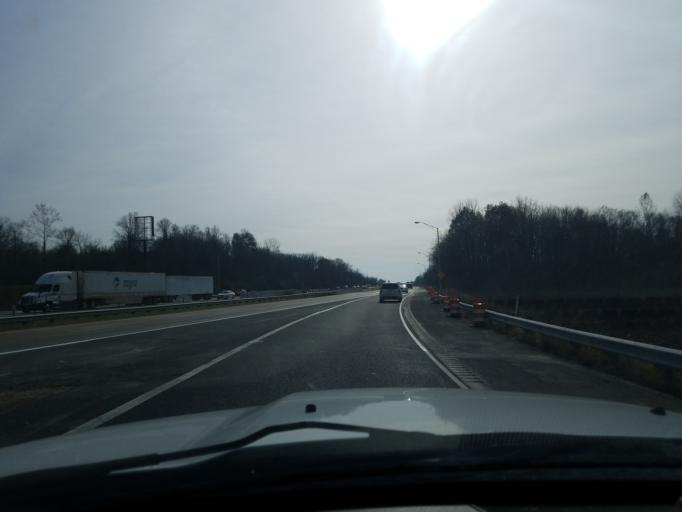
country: US
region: Indiana
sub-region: Delaware County
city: Yorktown
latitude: 40.2171
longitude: -85.5611
